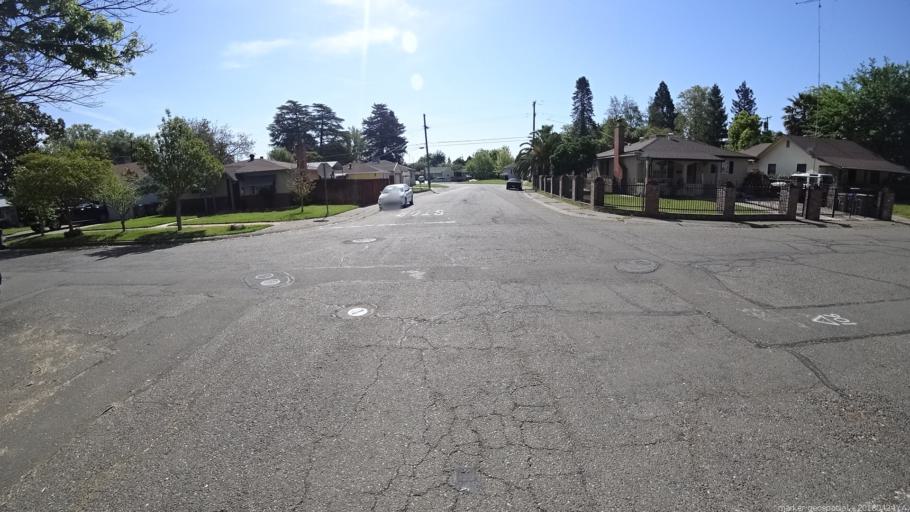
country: US
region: California
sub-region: Yolo County
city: West Sacramento
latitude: 38.5659
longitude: -121.5289
